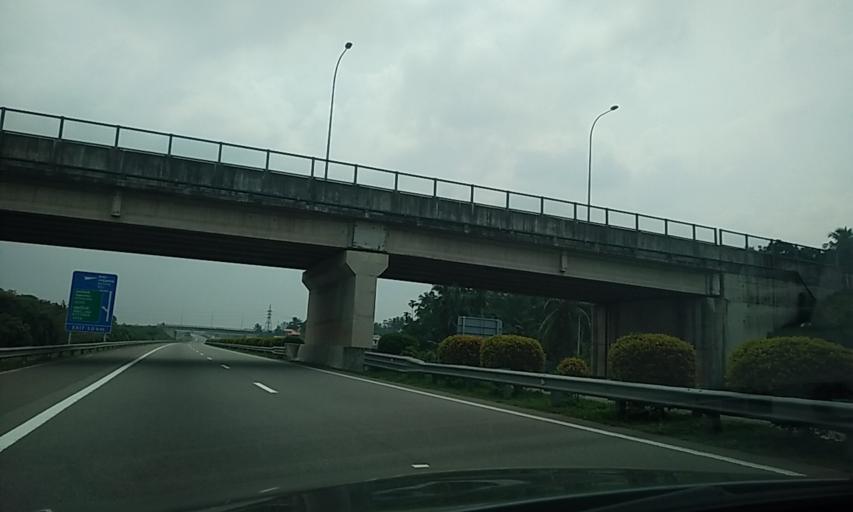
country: LK
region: Western
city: Homagama
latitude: 6.8527
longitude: 79.9784
